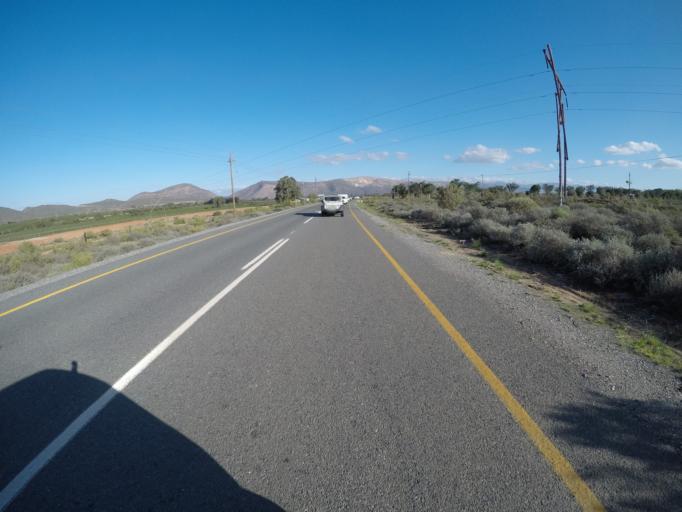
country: ZA
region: Western Cape
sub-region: Cape Winelands District Municipality
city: Ashton
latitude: -33.7923
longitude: 19.7799
